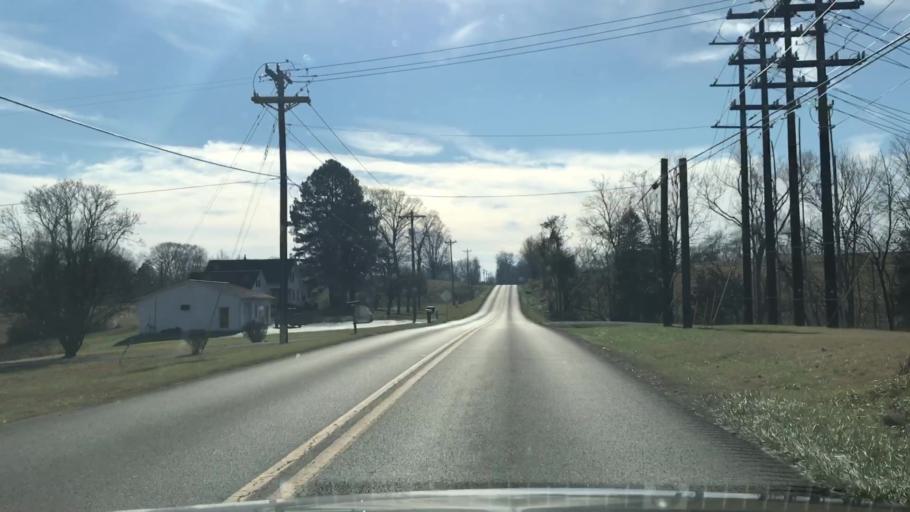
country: US
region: Kentucky
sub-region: Metcalfe County
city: Edmonton
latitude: 36.9552
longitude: -85.6138
